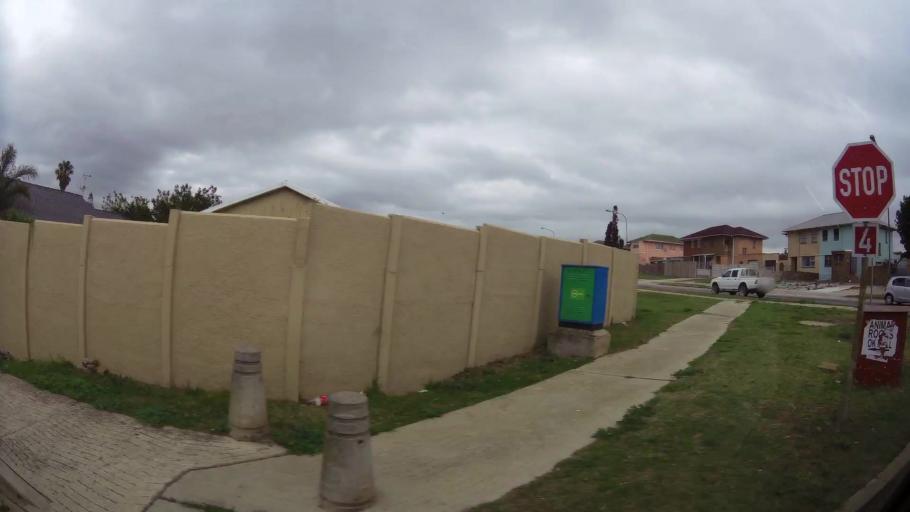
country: ZA
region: Eastern Cape
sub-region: Nelson Mandela Bay Metropolitan Municipality
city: Port Elizabeth
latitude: -33.9083
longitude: 25.5693
